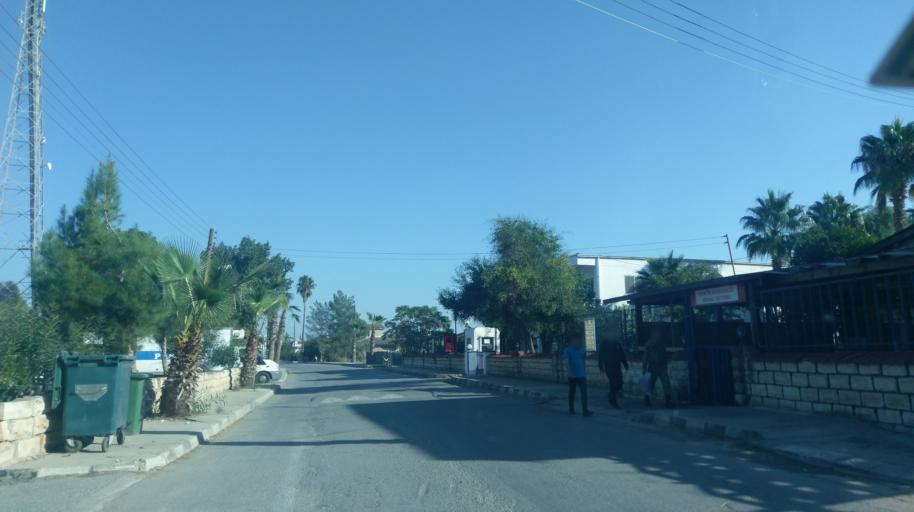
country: CY
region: Larnaka
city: Pergamos
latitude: 35.1096
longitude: 33.6809
